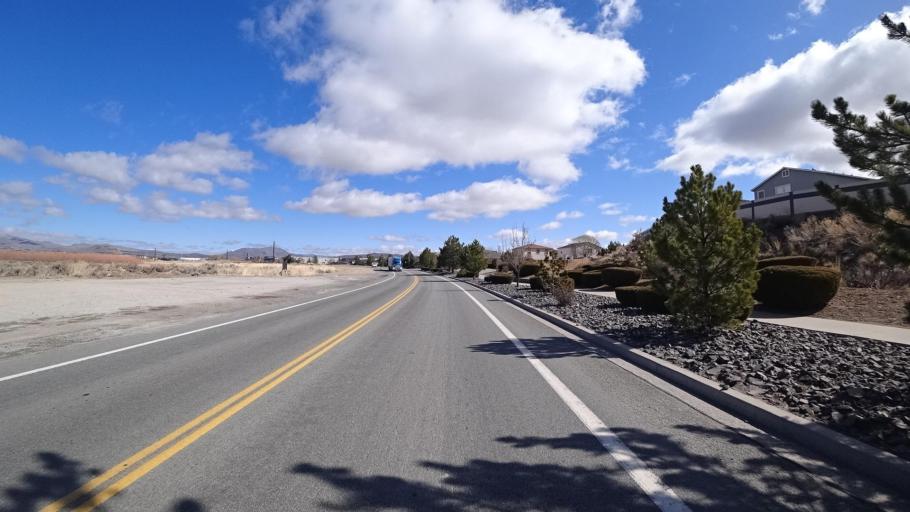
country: US
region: Nevada
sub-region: Washoe County
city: Lemmon Valley
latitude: 39.6362
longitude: -119.8984
